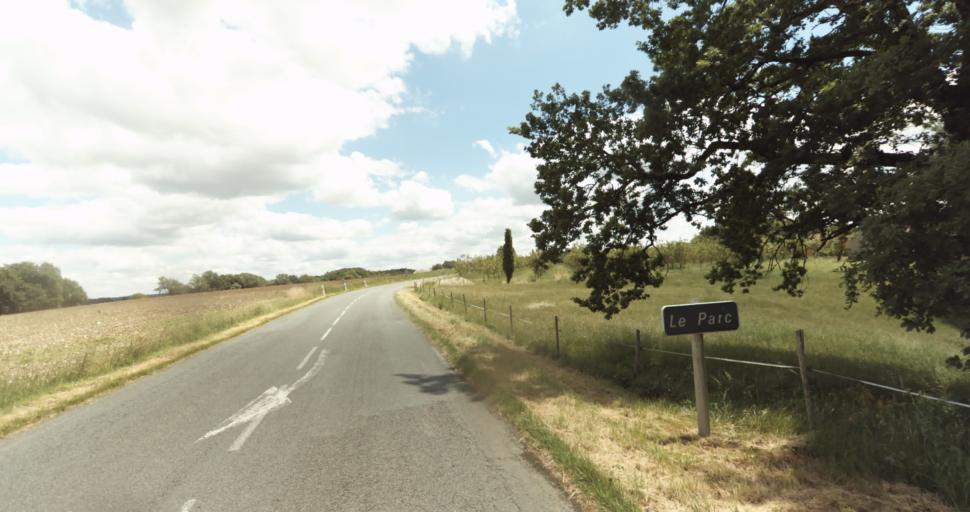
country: FR
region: Aquitaine
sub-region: Departement de la Dordogne
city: Beaumont-du-Perigord
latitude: 44.7013
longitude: 0.8433
